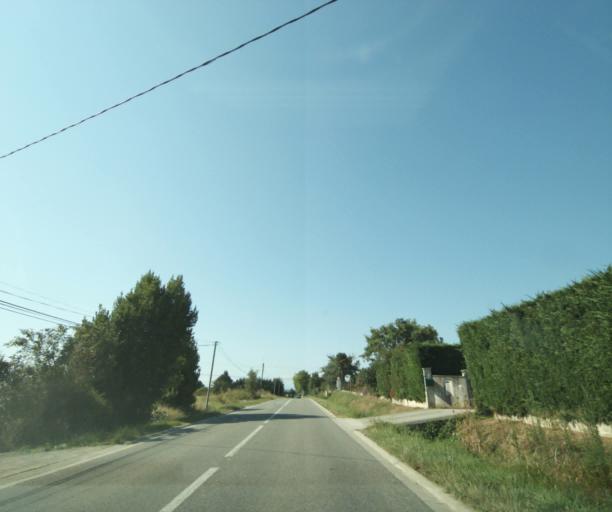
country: FR
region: Midi-Pyrenees
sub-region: Departement de la Haute-Garonne
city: Beaumont-sur-Leze
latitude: 43.3644
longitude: 1.3296
